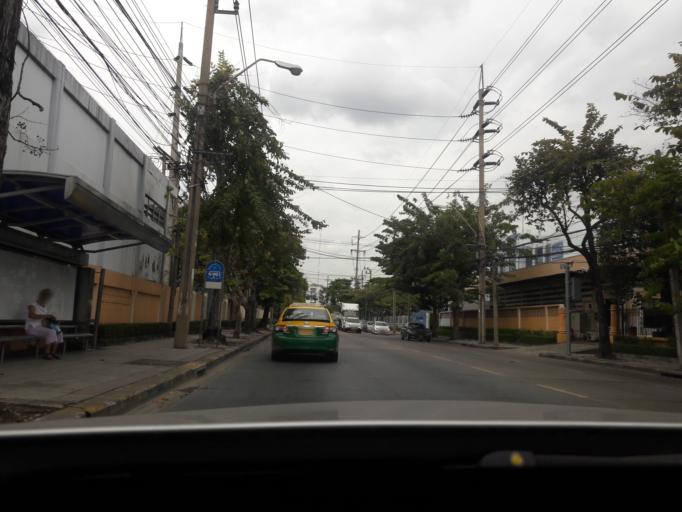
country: TH
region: Bangkok
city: Dusit
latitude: 13.7756
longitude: 100.5301
